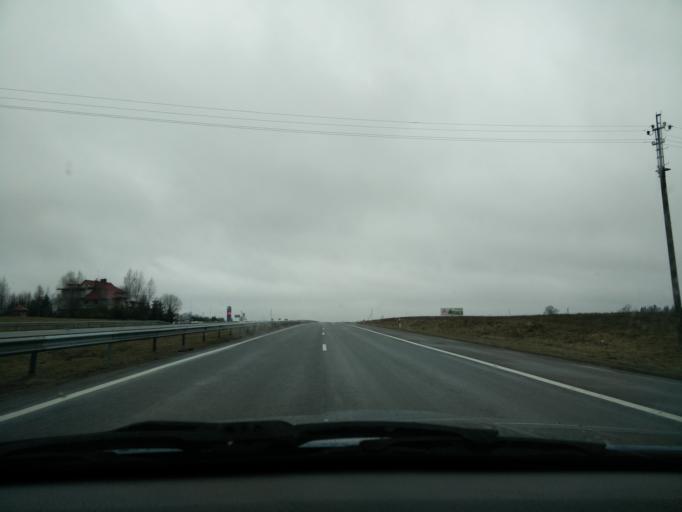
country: LT
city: Silale
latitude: 55.5202
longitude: 22.3698
